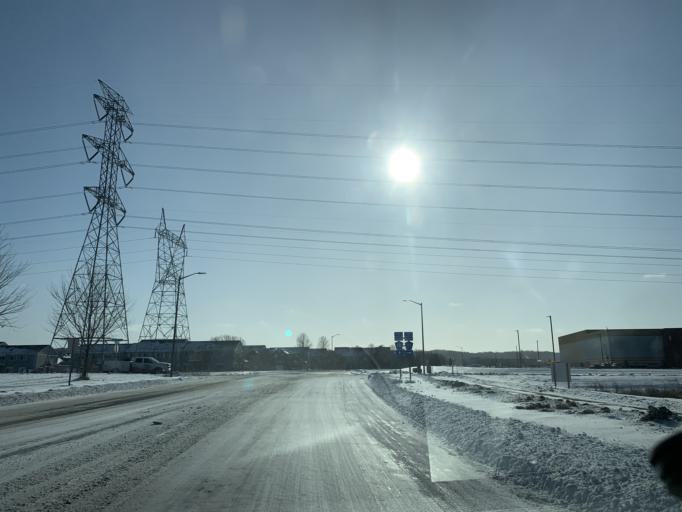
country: US
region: Minnesota
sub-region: Scott County
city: Prior Lake
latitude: 44.7782
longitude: -93.4092
